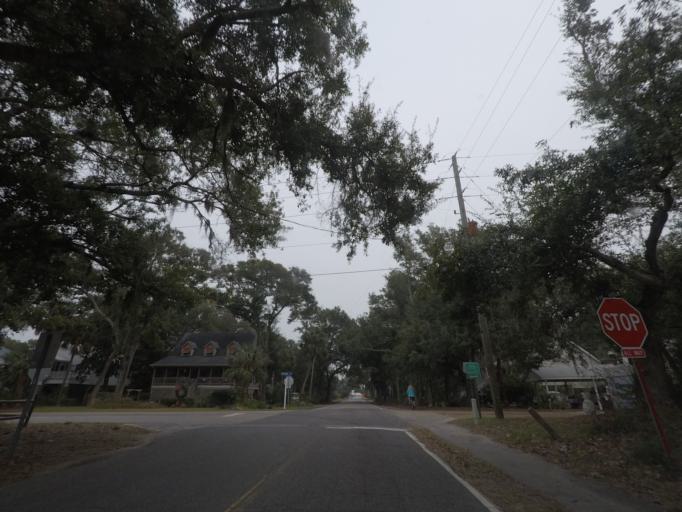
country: US
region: South Carolina
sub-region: Charleston County
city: Seabrook Island
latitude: 32.4884
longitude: -80.3247
